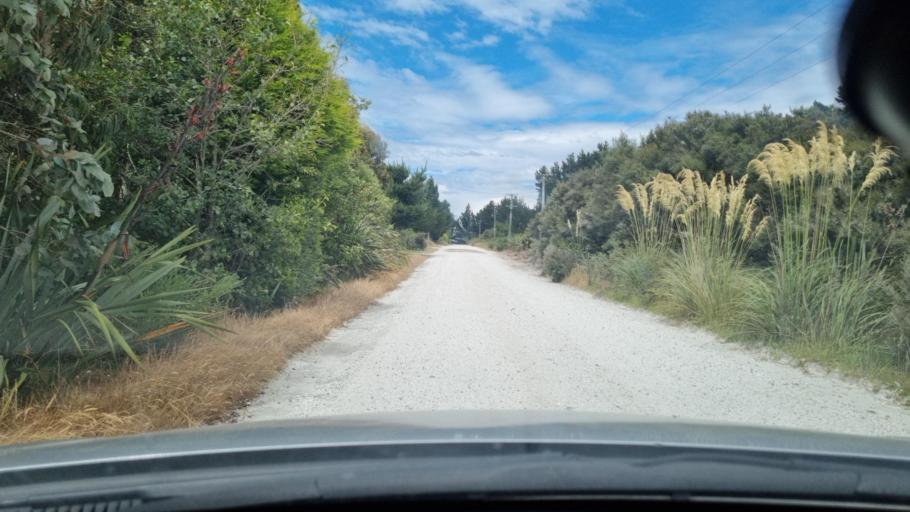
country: NZ
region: Southland
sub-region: Invercargill City
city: Bluff
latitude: -46.5572
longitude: 168.4335
